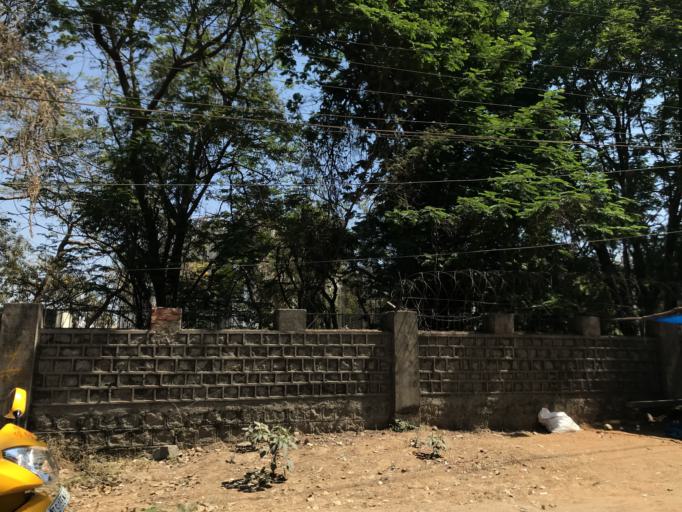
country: IN
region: Telangana
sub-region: Medak
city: Serilingampalle
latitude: 17.4678
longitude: 78.3316
